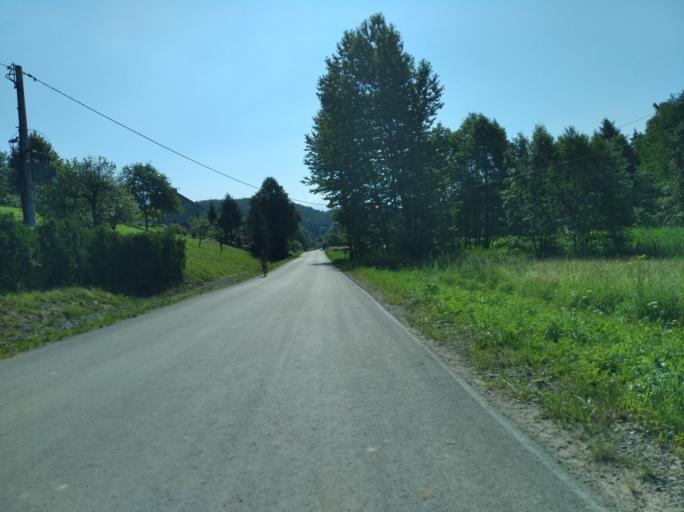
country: PL
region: Subcarpathian Voivodeship
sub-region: Powiat brzozowski
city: Wesola
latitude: 49.8271
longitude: 22.1549
